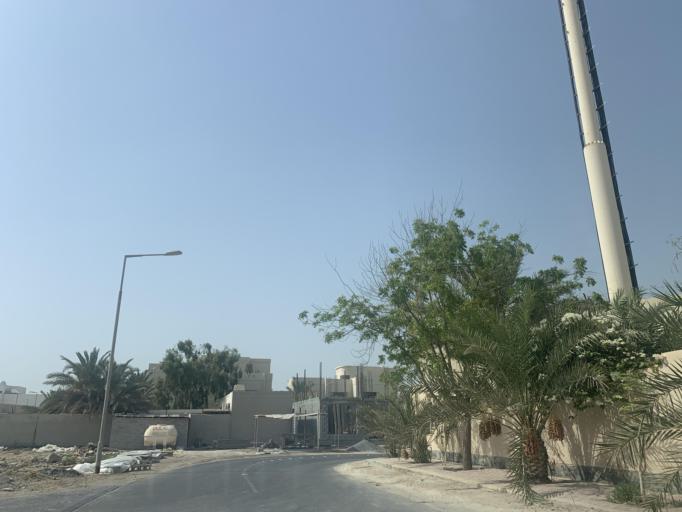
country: BH
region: Northern
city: Madinat `Isa
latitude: 26.1936
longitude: 50.4938
